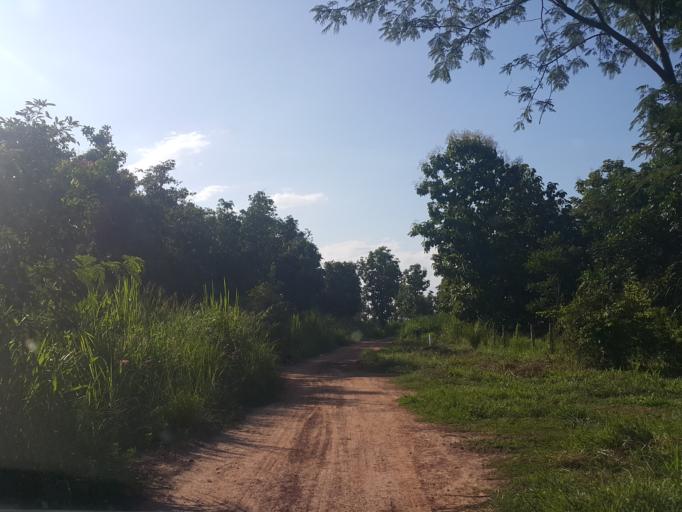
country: TH
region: Chiang Mai
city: Mae On
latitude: 18.7120
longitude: 99.2078
